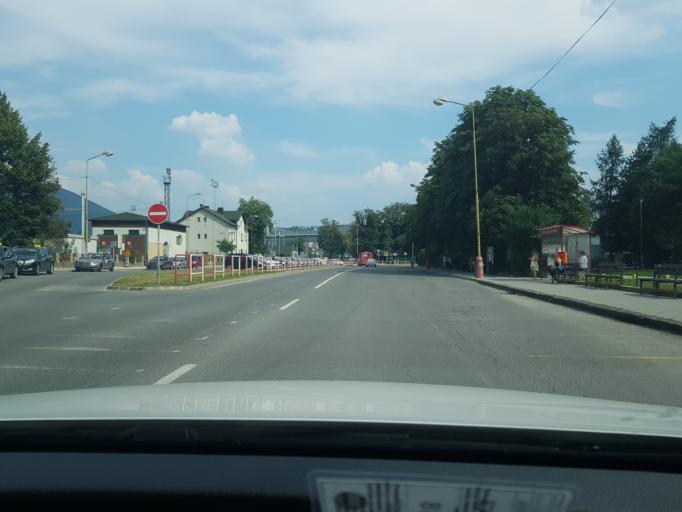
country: SK
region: Trenciansky
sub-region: Okres Povazska Bystrica
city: Povazska Bystrica
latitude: 49.1221
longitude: 18.4319
